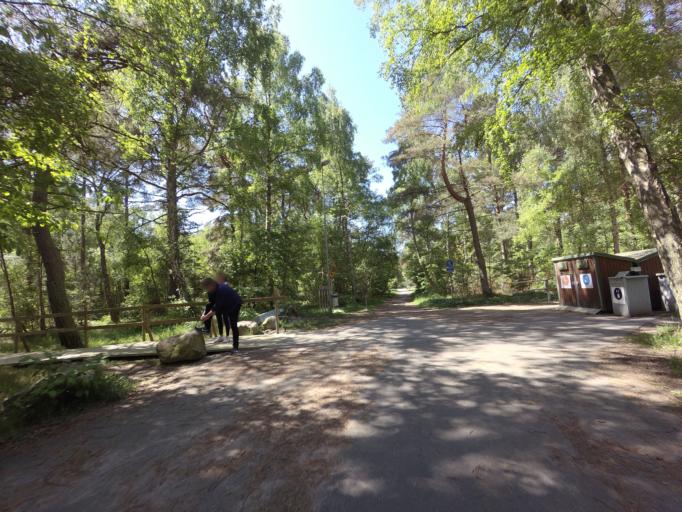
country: SE
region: Skane
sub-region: Vellinge Kommun
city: Hollviken
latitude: 55.4037
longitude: 12.9629
